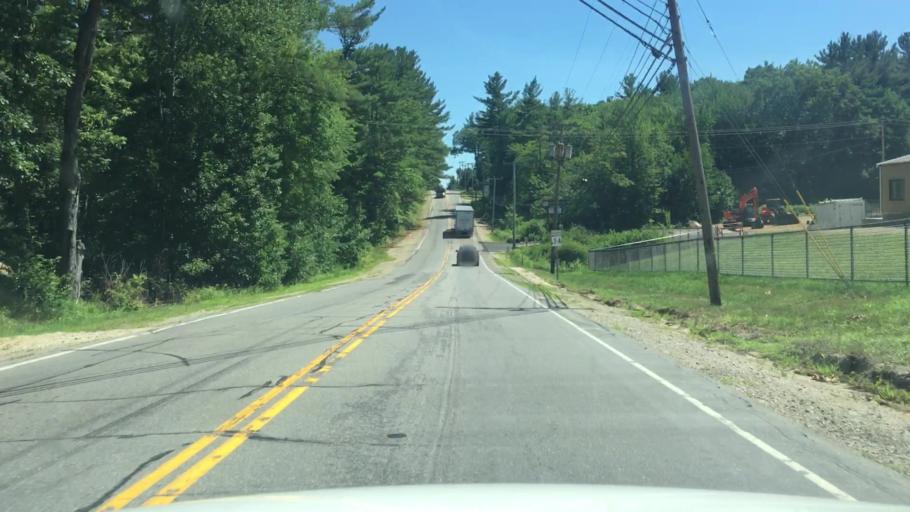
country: US
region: New Hampshire
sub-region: Merrimack County
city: Suncook
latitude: 43.1256
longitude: -71.4811
